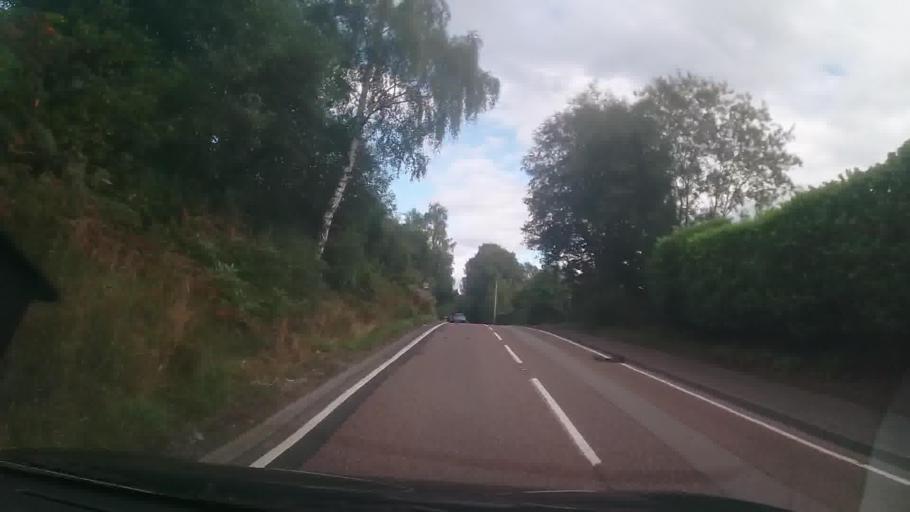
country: GB
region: Scotland
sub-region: Argyll and Bute
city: Garelochhead
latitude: 56.3939
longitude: -5.0591
